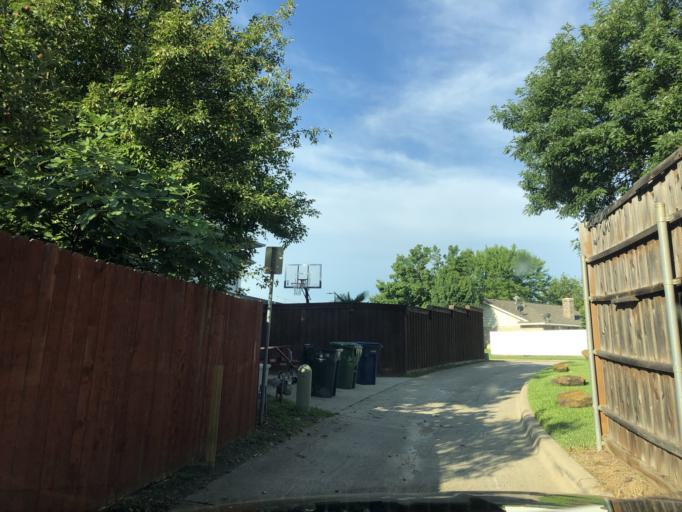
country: US
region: Texas
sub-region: Dallas County
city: Sunnyvale
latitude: 32.8422
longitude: -96.6097
